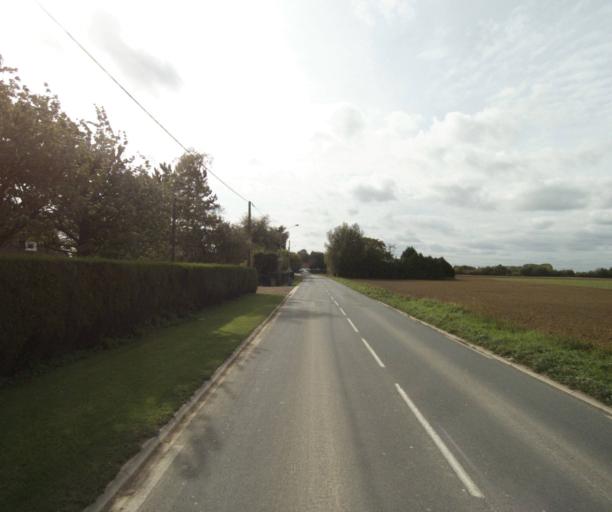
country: FR
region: Nord-Pas-de-Calais
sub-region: Departement du Nord
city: Bois-Grenier
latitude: 50.6552
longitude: 2.8844
